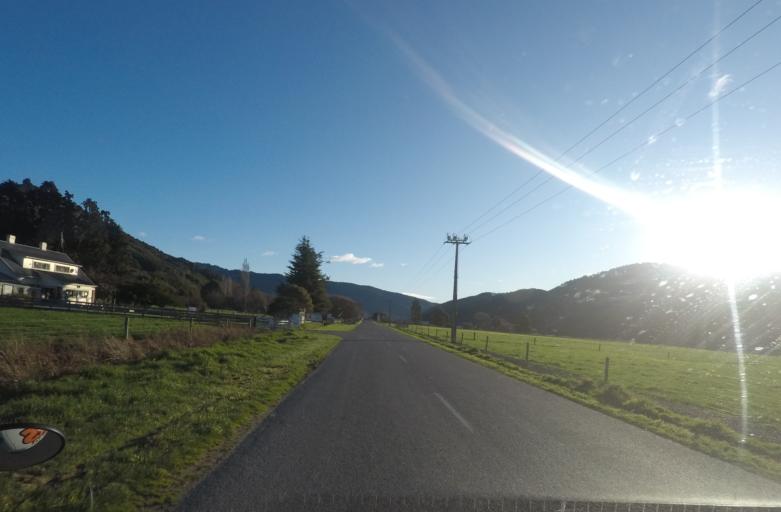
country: NZ
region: Marlborough
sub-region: Marlborough District
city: Picton
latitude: -41.2892
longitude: 173.8582
